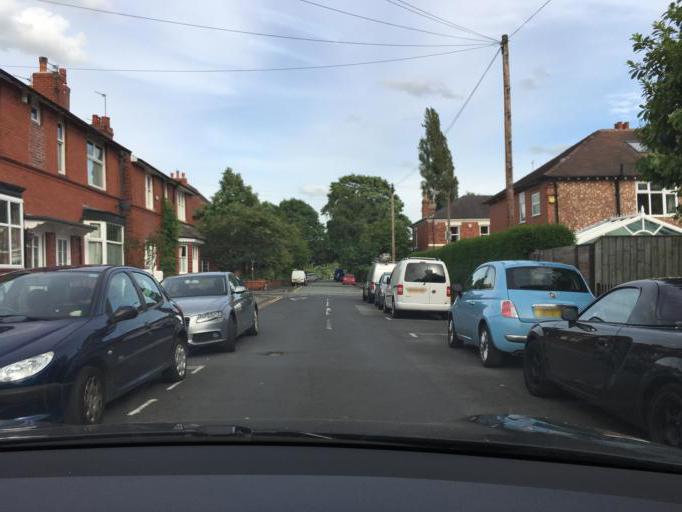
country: GB
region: England
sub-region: Borough of Stockport
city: Hazel Grove
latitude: 53.3810
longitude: -2.1189
